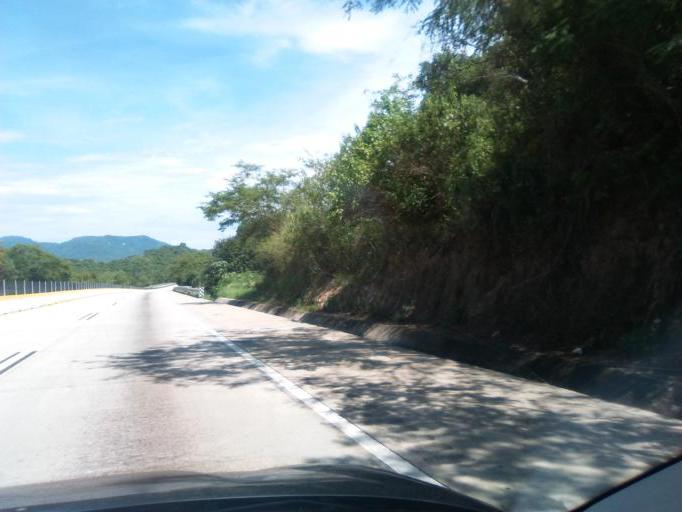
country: MX
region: Guerrero
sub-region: Acapulco de Juarez
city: Kilometro 30
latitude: 16.9754
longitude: -99.7222
